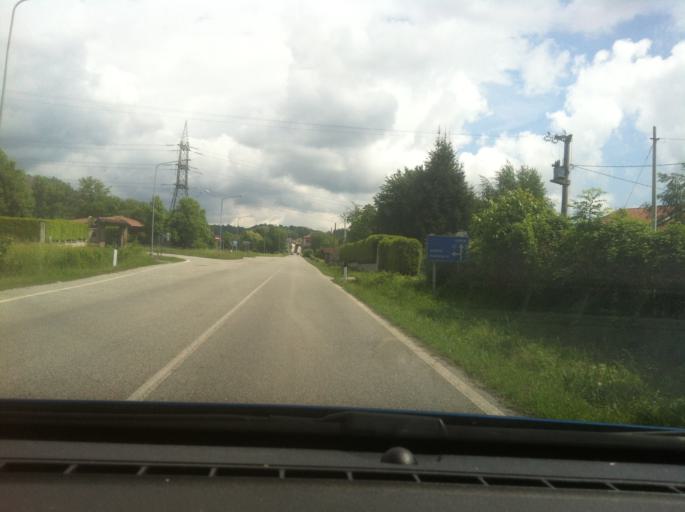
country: IT
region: Piedmont
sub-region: Provincia di Torino
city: Baldissero Canavese
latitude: 45.3989
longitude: 7.7372
